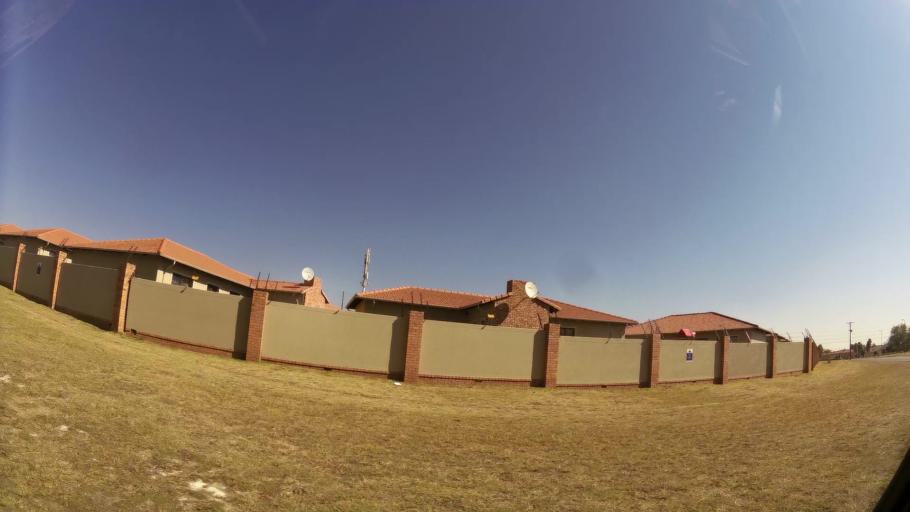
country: ZA
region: Gauteng
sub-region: City of Johannesburg Metropolitan Municipality
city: Midrand
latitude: -25.9659
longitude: 28.1160
